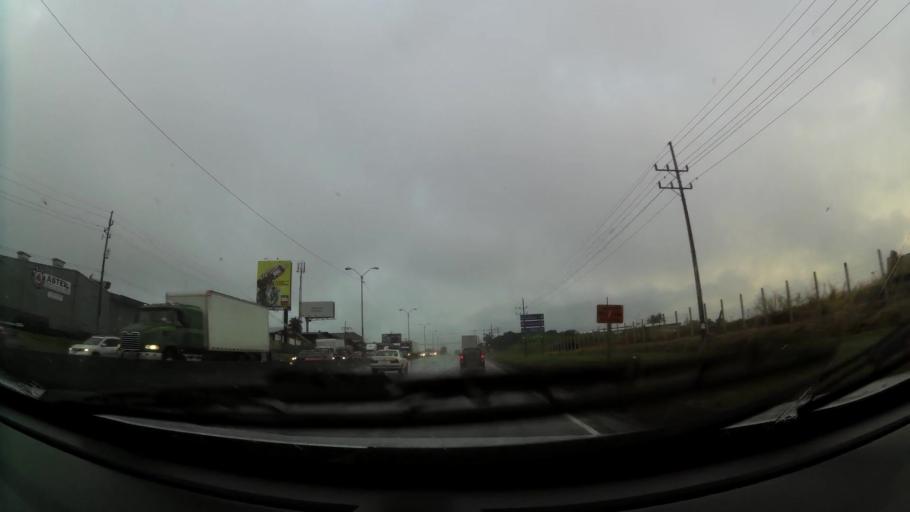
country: CR
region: Heredia
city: La Asuncion
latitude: 9.9856
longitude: -84.1641
